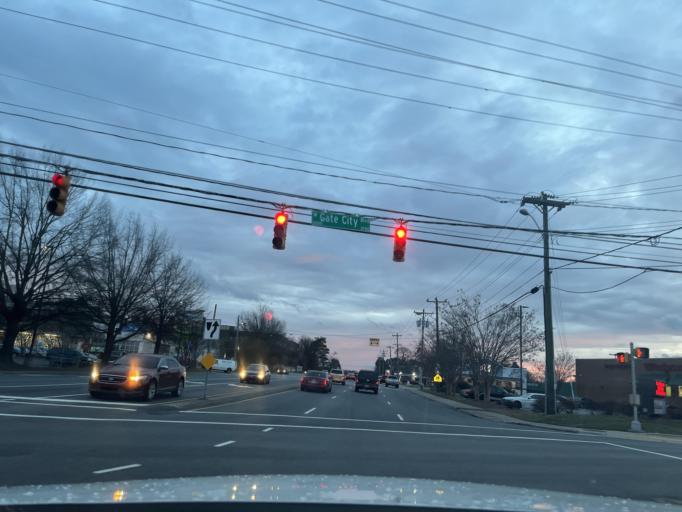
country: US
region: North Carolina
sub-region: Guilford County
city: Greensboro
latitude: 36.0398
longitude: -79.8498
